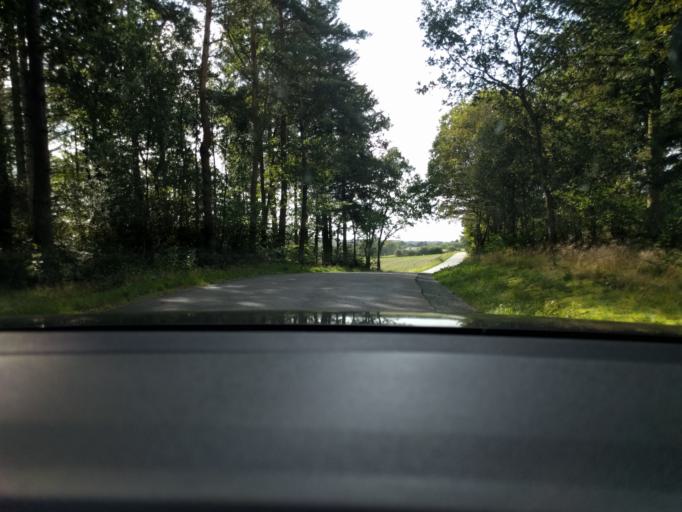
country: DK
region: Central Jutland
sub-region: Silkeborg Kommune
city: Silkeborg
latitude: 56.2718
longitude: 9.5998
